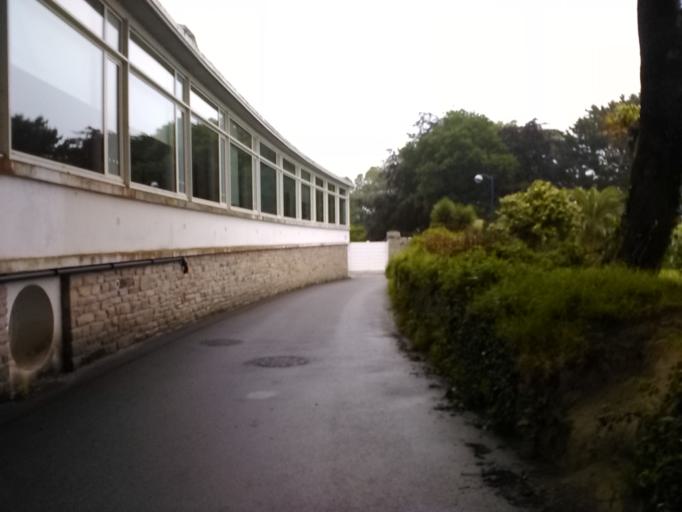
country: FR
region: Brittany
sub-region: Departement du Finistere
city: Fouesnant
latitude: 47.8605
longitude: -3.9847
